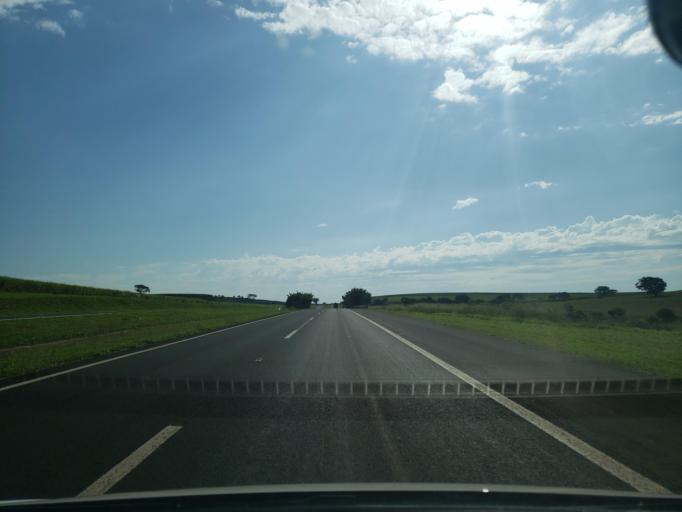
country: BR
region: Sao Paulo
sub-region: Promissao
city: Promissao
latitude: -21.5489
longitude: -49.9587
